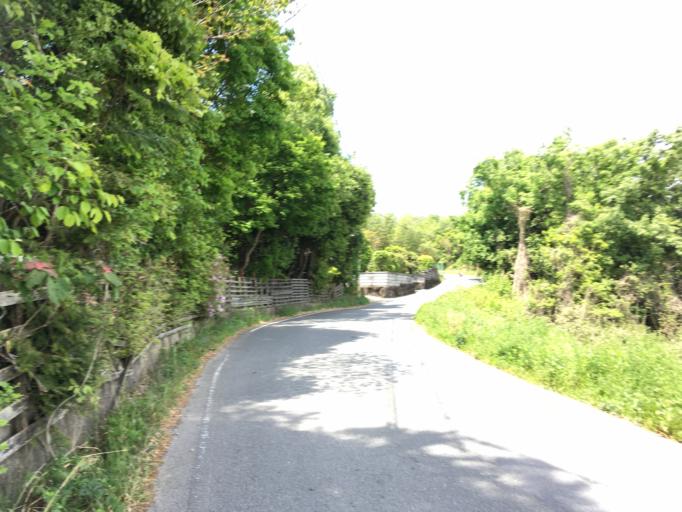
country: JP
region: Nara
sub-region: Ikoma-shi
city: Ikoma
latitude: 34.6508
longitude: 135.6964
